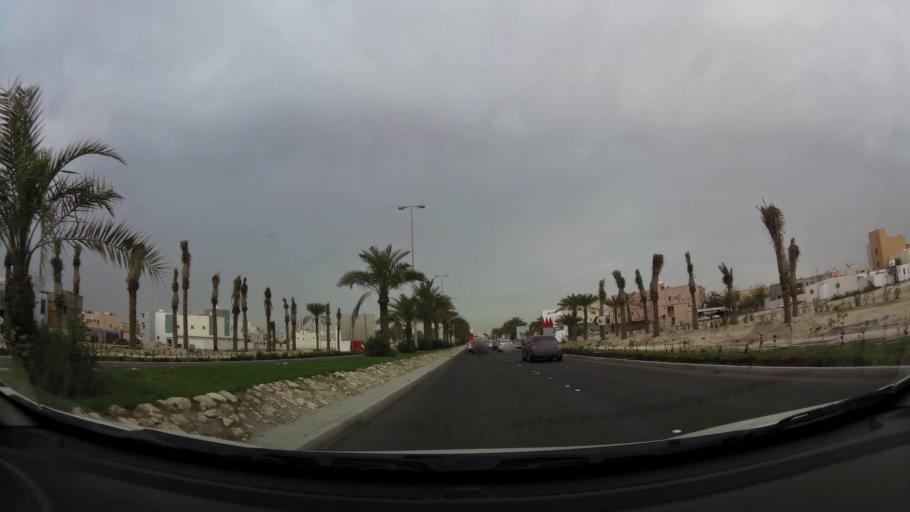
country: BH
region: Central Governorate
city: Dar Kulayb
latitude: 26.0598
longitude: 50.5085
